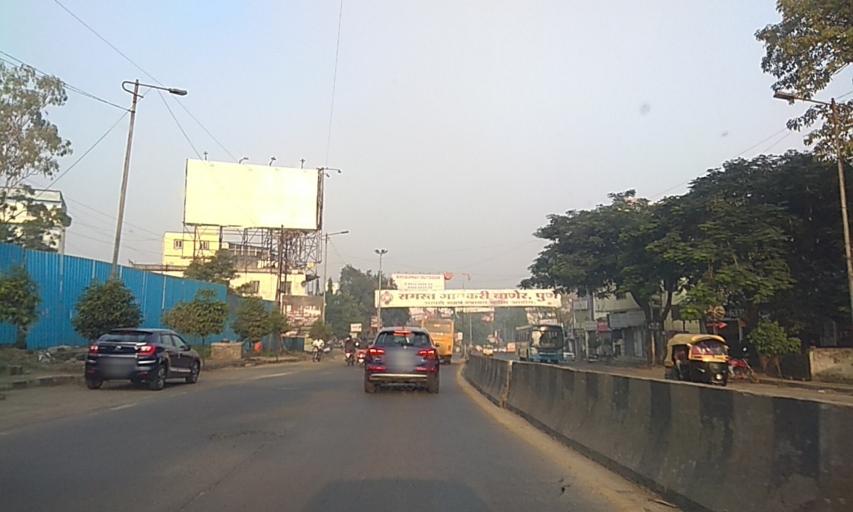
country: IN
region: Maharashtra
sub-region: Pune Division
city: Khadki
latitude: 18.5597
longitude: 73.7896
